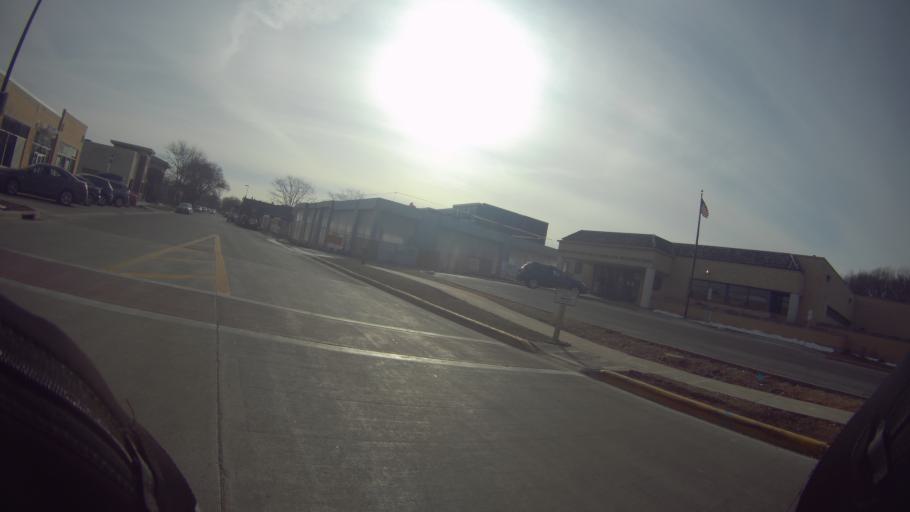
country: US
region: Wisconsin
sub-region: Dane County
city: Middleton
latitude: 43.0959
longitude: -89.5139
